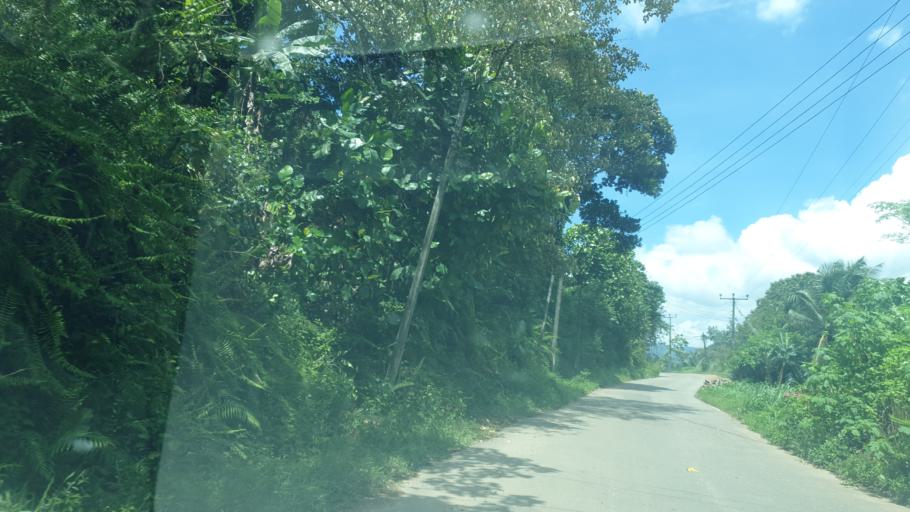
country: LK
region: Sabaragamuwa
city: Ratnapura
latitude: 6.4713
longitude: 80.4234
